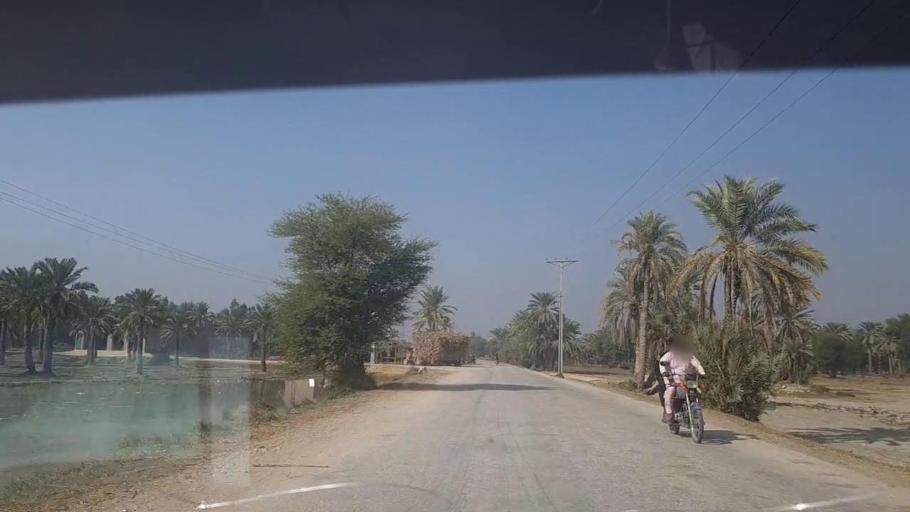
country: PK
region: Sindh
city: Kot Diji
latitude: 27.3619
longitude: 68.7070
